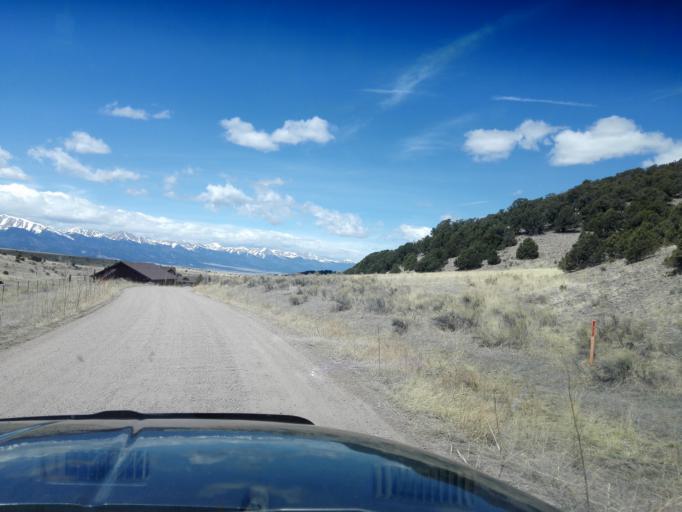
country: US
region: Colorado
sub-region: Custer County
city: Westcliffe
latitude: 37.9770
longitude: -105.2937
